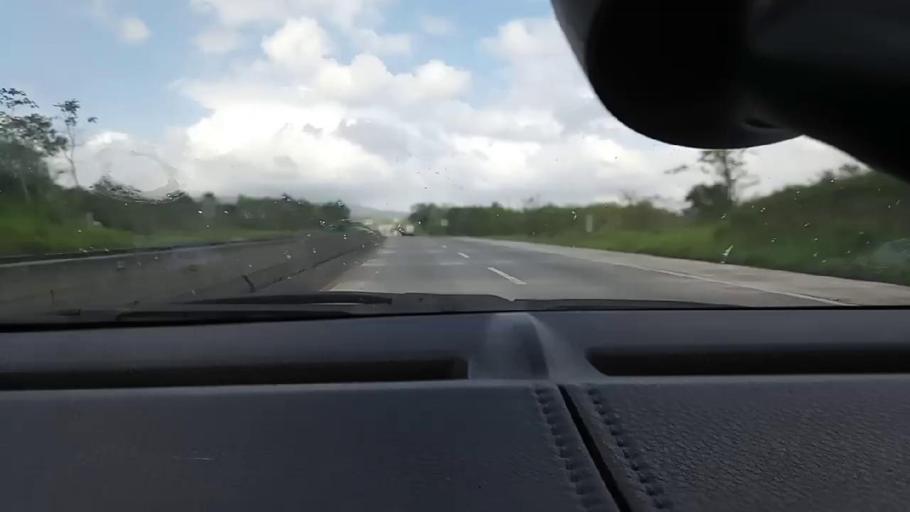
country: PA
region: Colon
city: Nuevo San Juan
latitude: 9.1872
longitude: -79.6432
